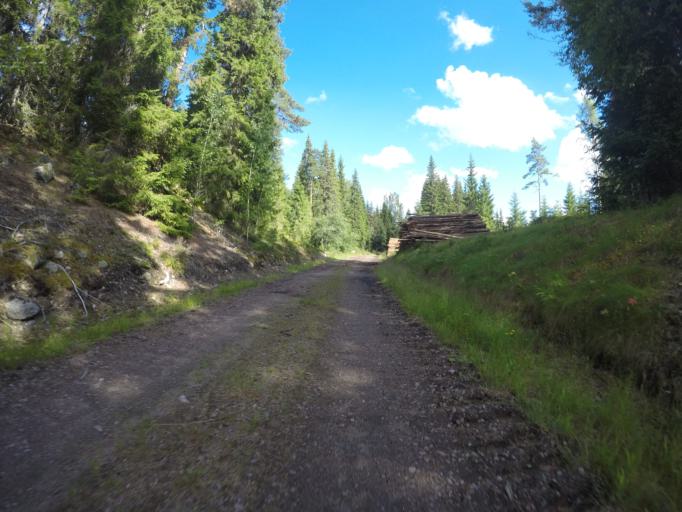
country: SE
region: Dalarna
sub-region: Ludvika Kommun
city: Abborrberget
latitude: 60.0275
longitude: 14.6161
